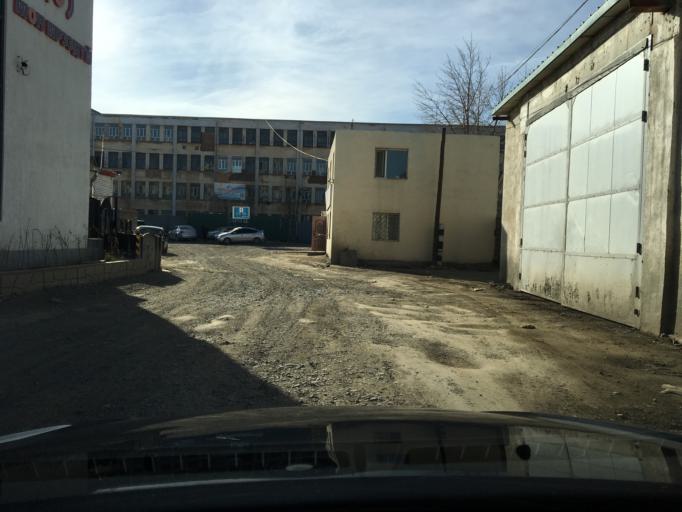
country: MN
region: Ulaanbaatar
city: Ulaanbaatar
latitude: 47.8943
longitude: 106.8931
